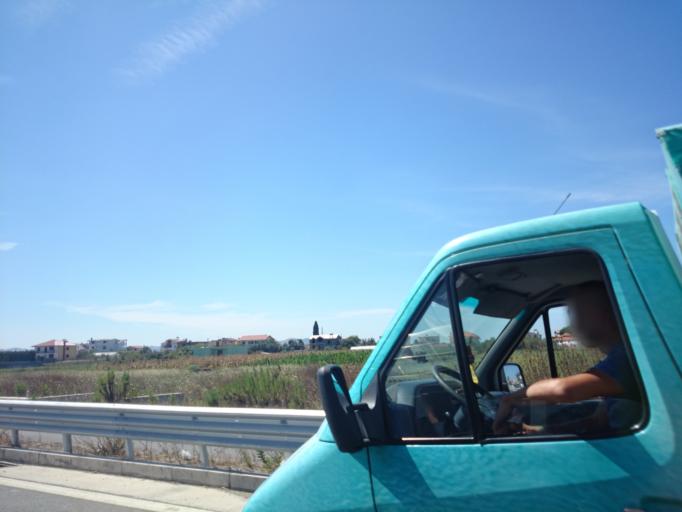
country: AL
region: Tirane
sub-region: Rrethi i Kavajes
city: Golem
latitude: 41.2216
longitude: 19.5283
